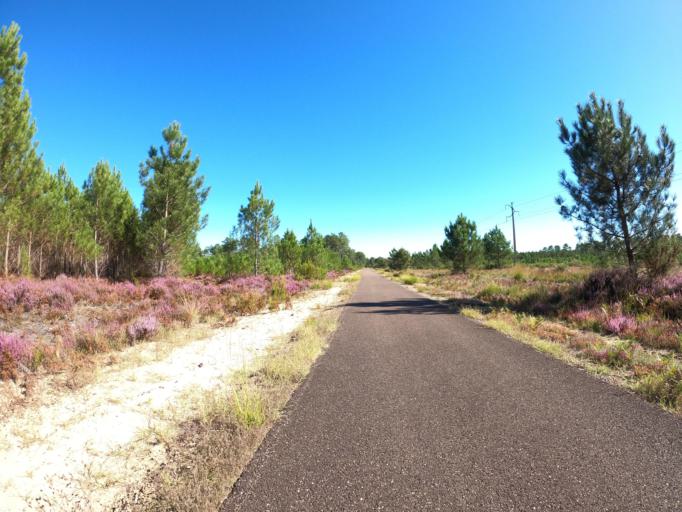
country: FR
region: Aquitaine
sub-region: Departement des Landes
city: Ychoux
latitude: 44.3379
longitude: -0.9564
